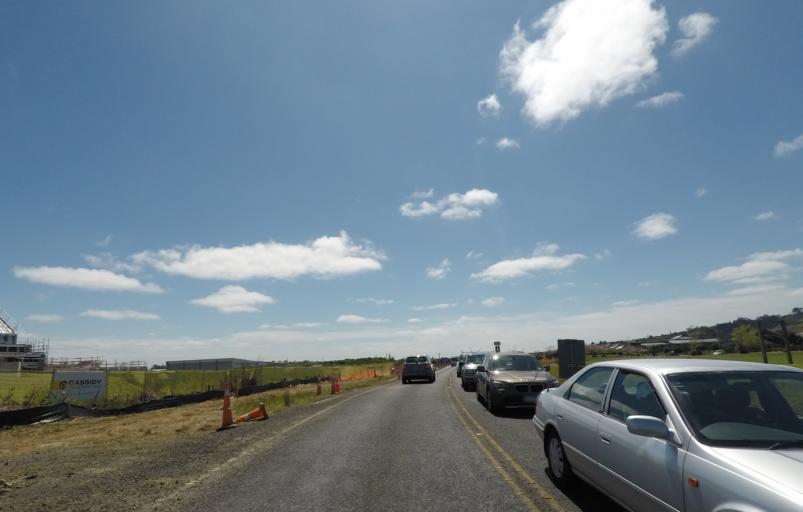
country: NZ
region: Auckland
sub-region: Auckland
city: Manukau City
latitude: -36.9614
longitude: 174.9076
